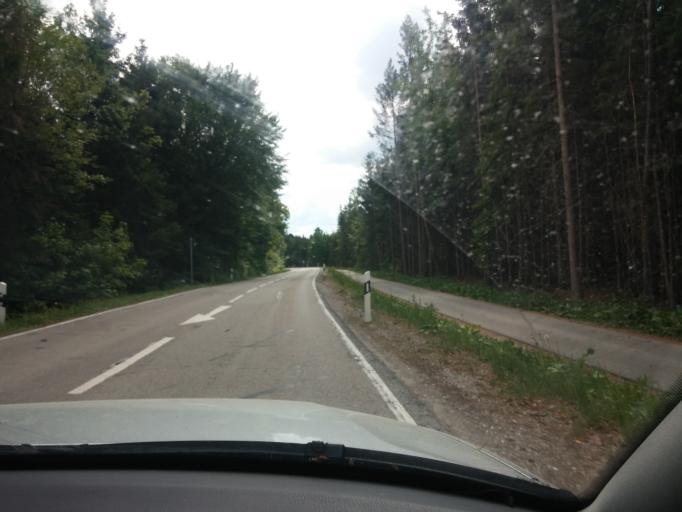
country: DE
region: Bavaria
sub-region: Upper Bavaria
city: Hohenkirchen-Siegertsbrunn
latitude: 48.0066
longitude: 11.7088
